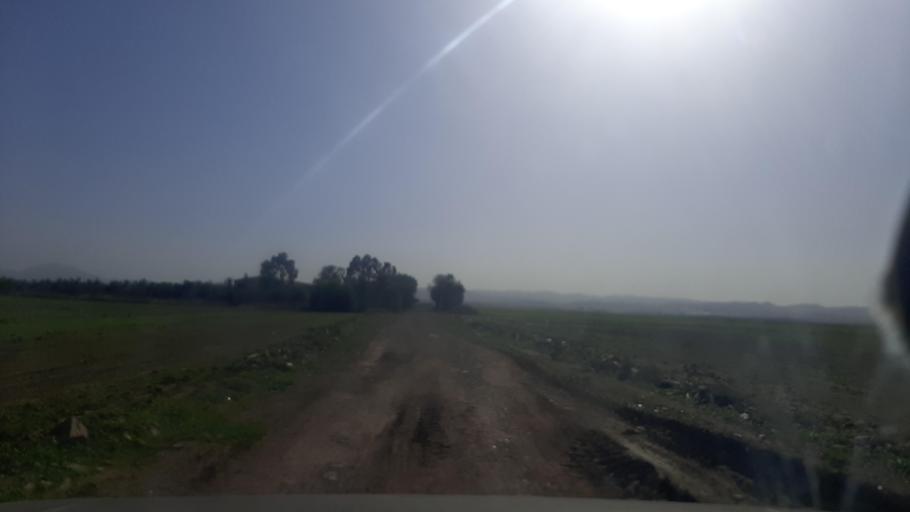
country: TN
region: Tunis
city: La Mohammedia
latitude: 36.6446
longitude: 10.0912
